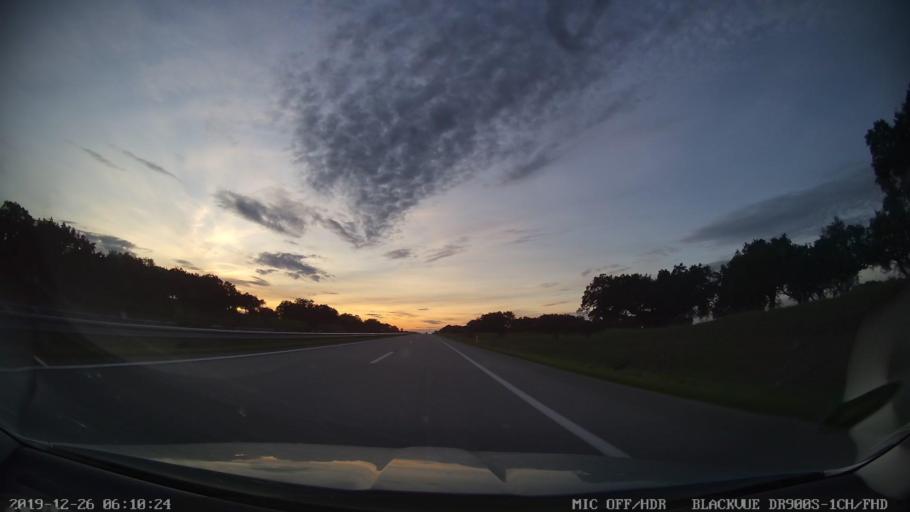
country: PT
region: Evora
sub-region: Montemor-O-Novo
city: Montemor-o-Novo
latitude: 38.6721
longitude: -8.1924
